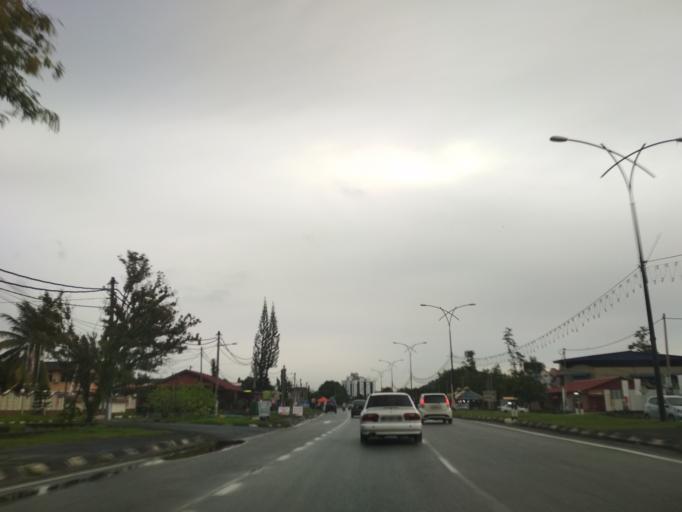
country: MY
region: Perlis
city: Kangar
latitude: 6.4517
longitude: 100.2063
